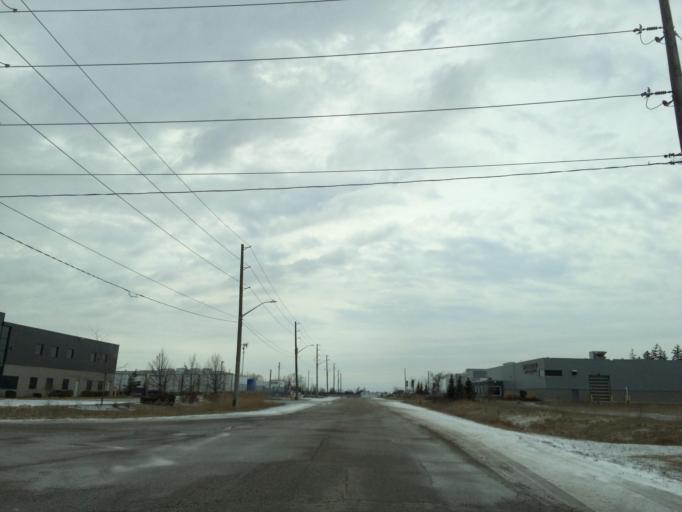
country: CA
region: Ontario
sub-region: Wellington County
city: Guelph
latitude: 43.5435
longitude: -80.3155
